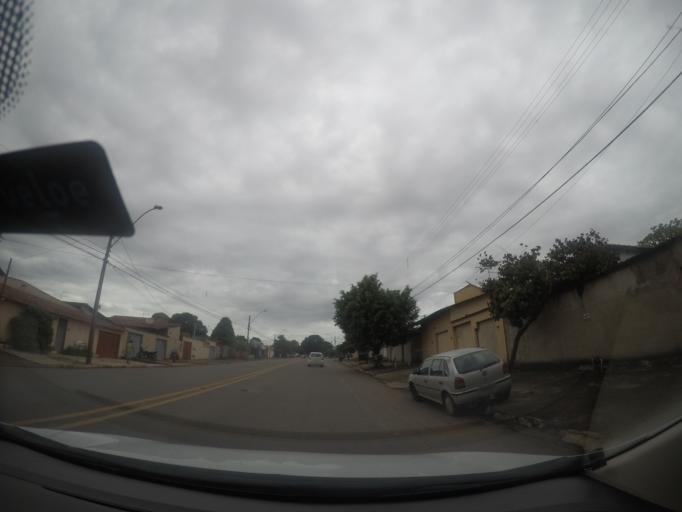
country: BR
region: Goias
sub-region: Goiania
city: Goiania
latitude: -16.6115
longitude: -49.2953
